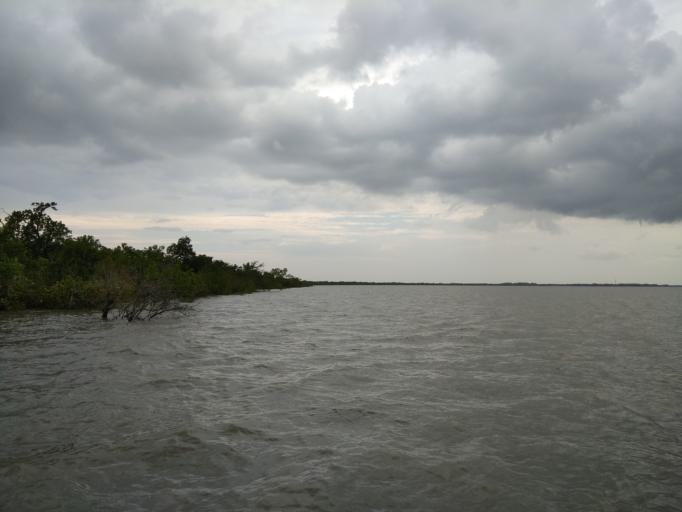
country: IN
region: West Bengal
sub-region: North 24 Parganas
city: Gosaba
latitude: 22.2188
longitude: 89.2411
